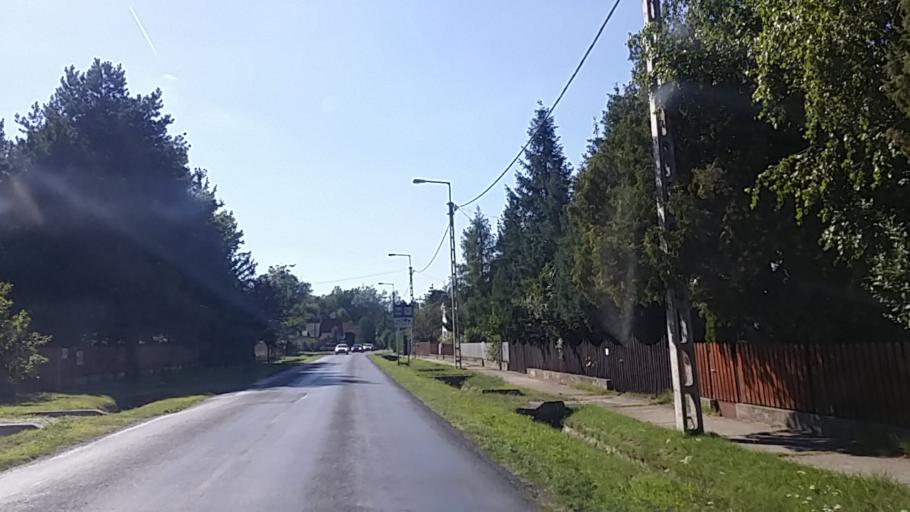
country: HU
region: Somogy
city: Balatonbereny
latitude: 46.7080
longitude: 17.3608
